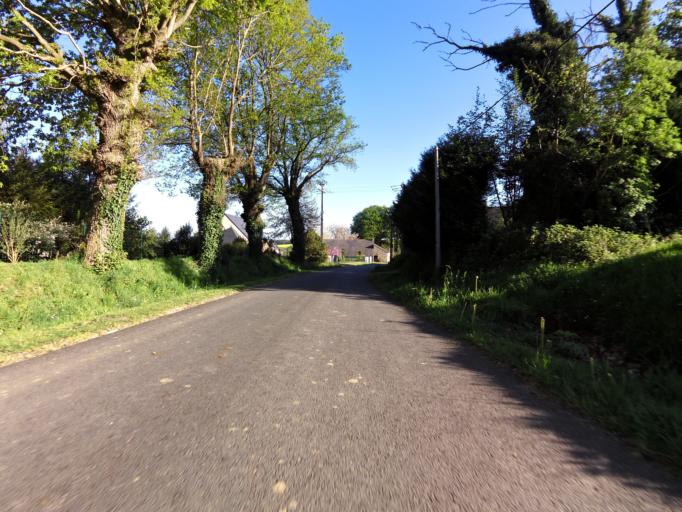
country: FR
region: Brittany
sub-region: Departement du Morbihan
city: Pluherlin
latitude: 47.7166
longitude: -2.3557
